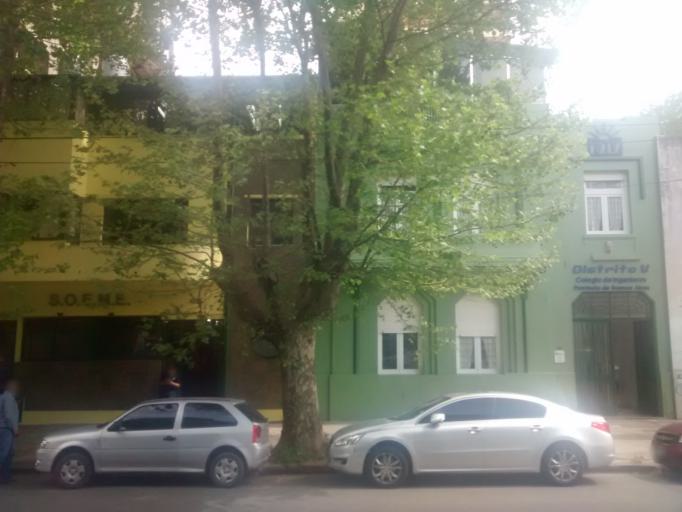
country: AR
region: Buenos Aires
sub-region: Partido de La Plata
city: La Plata
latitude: -34.9118
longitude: -57.9401
